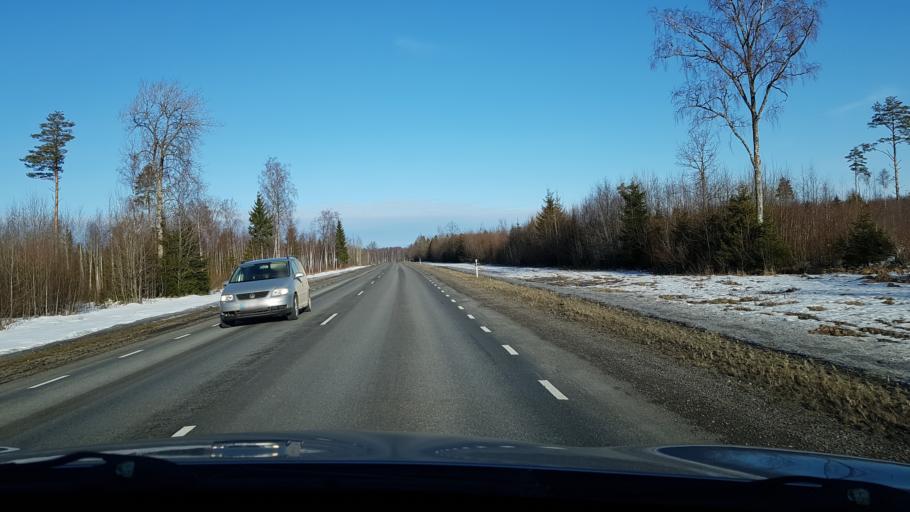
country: EE
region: Viljandimaa
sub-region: Vohma linn
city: Vohma
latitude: 58.6138
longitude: 25.5710
